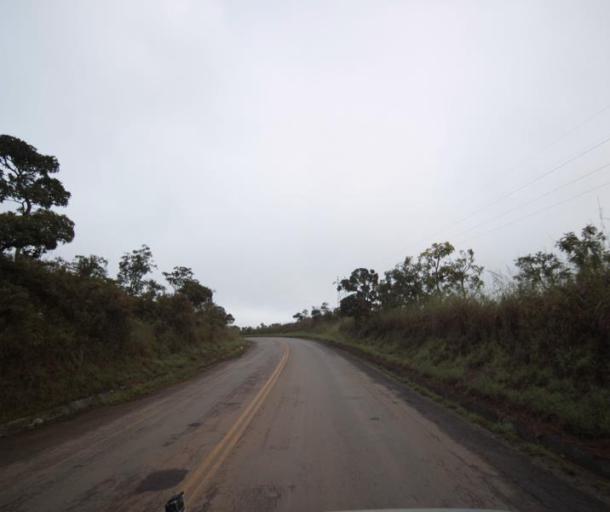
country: BR
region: Goias
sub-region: Pirenopolis
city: Pirenopolis
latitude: -15.8427
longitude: -48.7704
